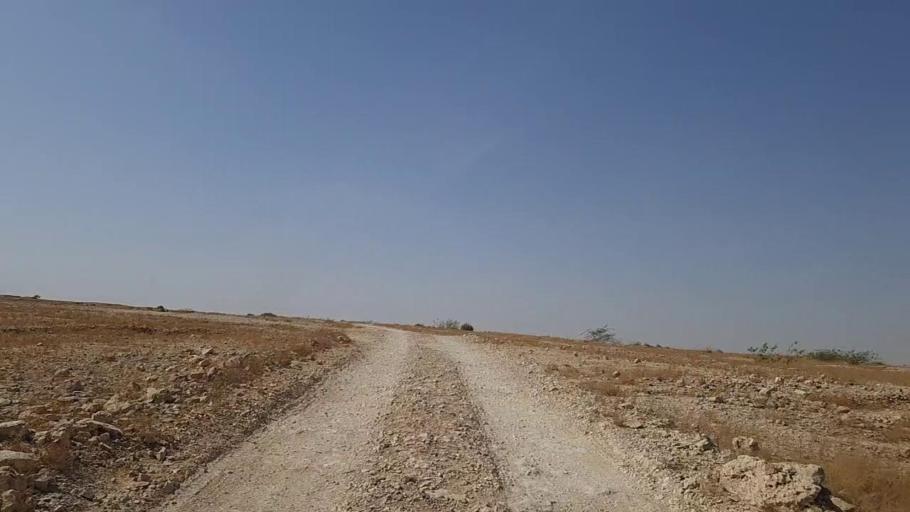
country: PK
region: Sindh
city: Kotri
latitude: 25.1642
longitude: 68.1902
